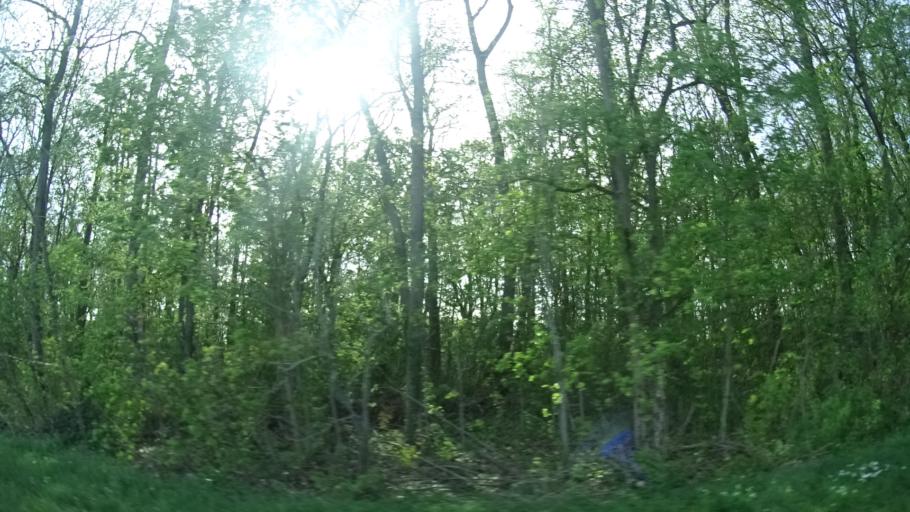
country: DE
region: Bavaria
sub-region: Regierungsbezirk Unterfranken
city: Kolitzheim
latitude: 49.8951
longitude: 10.2293
